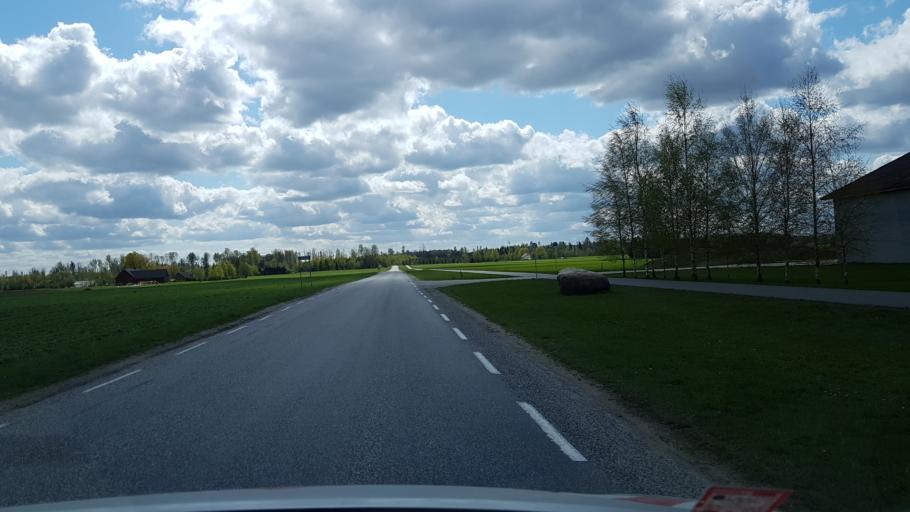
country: EE
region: Jogevamaa
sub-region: Poltsamaa linn
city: Poltsamaa
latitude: 58.7034
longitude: 25.9409
